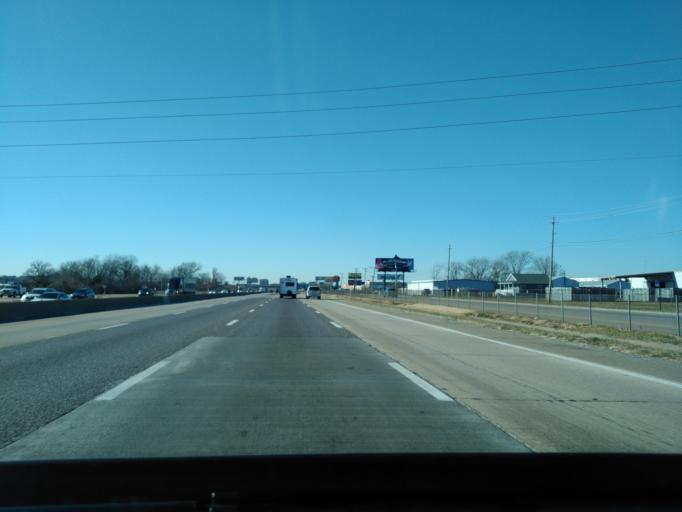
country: US
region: Missouri
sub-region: Saint Louis County
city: Fenton
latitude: 38.5429
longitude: -90.4439
